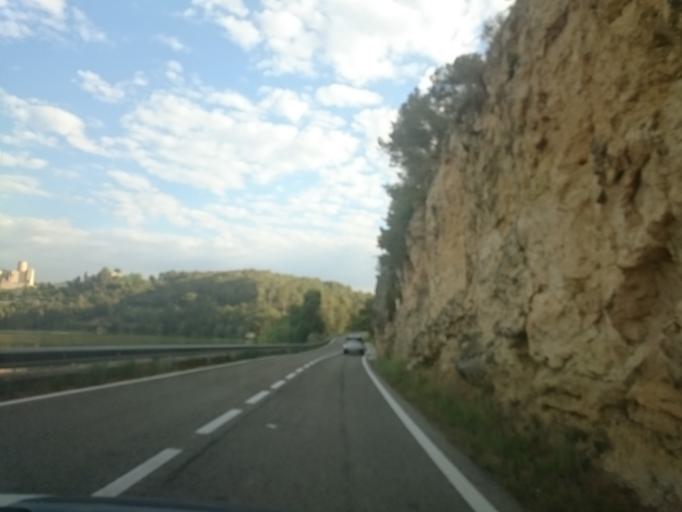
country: ES
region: Catalonia
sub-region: Provincia de Barcelona
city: Castellet
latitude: 41.2606
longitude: 1.6410
